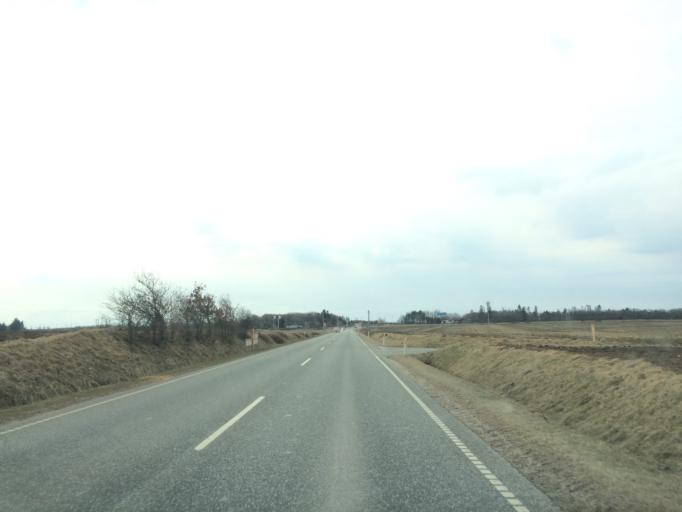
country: DK
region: Central Jutland
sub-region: Ringkobing-Skjern Kommune
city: Videbaek
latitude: 56.0913
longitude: 8.5075
